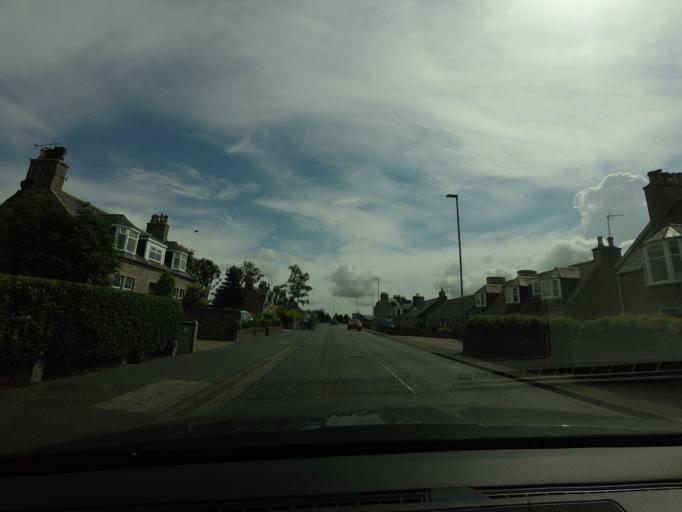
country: GB
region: Scotland
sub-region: Aberdeenshire
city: Mintlaw
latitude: 57.5251
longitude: -2.0037
